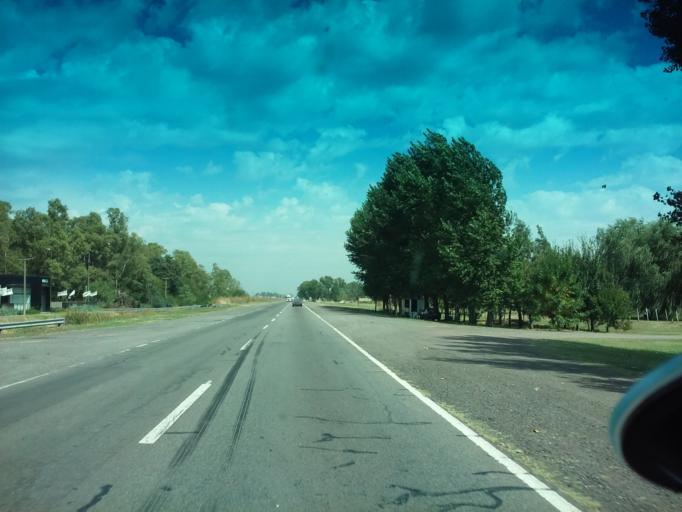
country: AR
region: Buenos Aires
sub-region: Partido de Carlos Casares
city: Carlos Casares
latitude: -35.6303
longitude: -61.3390
